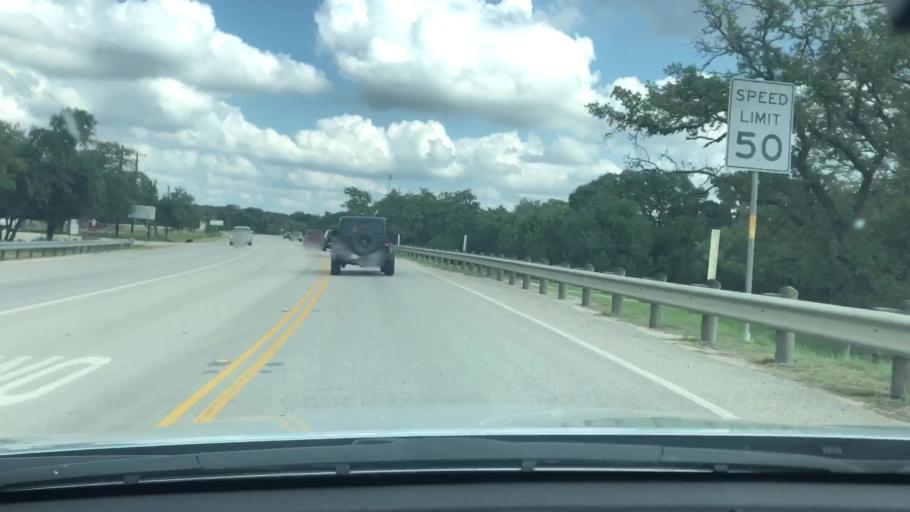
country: US
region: Texas
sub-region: Kendall County
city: Boerne
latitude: 29.7886
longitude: -98.7050
